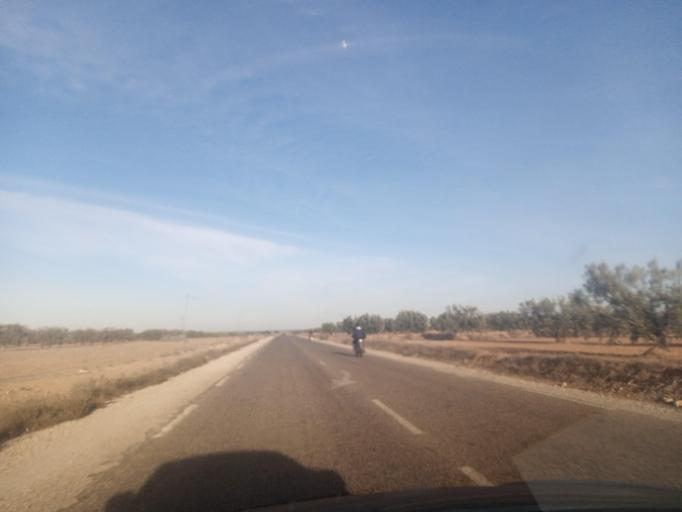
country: TN
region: Safaqis
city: Bi'r `Ali Bin Khalifah
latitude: 34.9316
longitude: 10.3267
